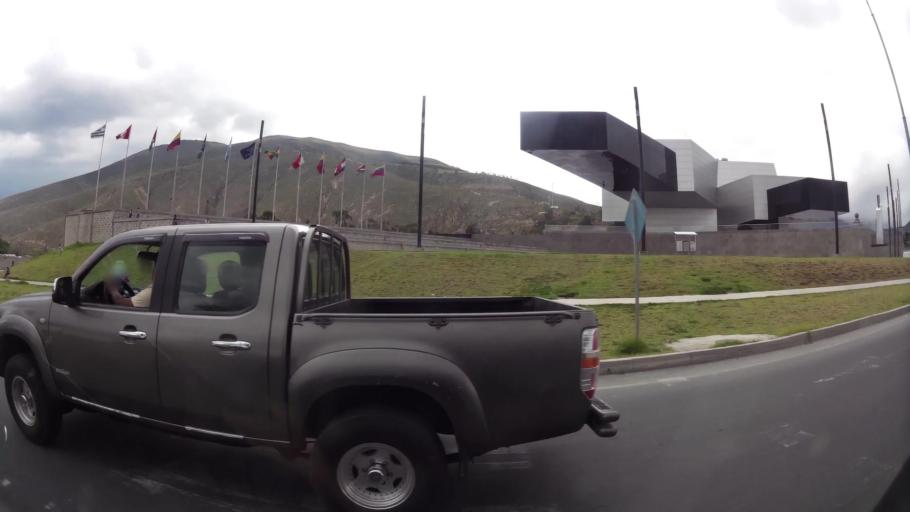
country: EC
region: Pichincha
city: Quito
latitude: -0.0047
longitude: -78.4531
